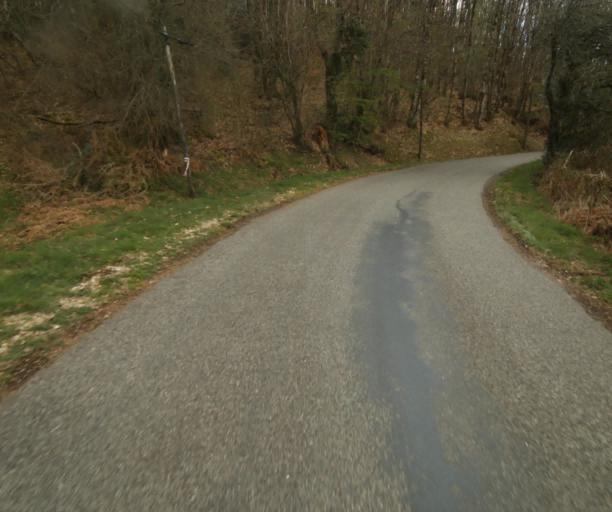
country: FR
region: Limousin
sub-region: Departement de la Correze
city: Laguenne
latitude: 45.2434
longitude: 1.8901
